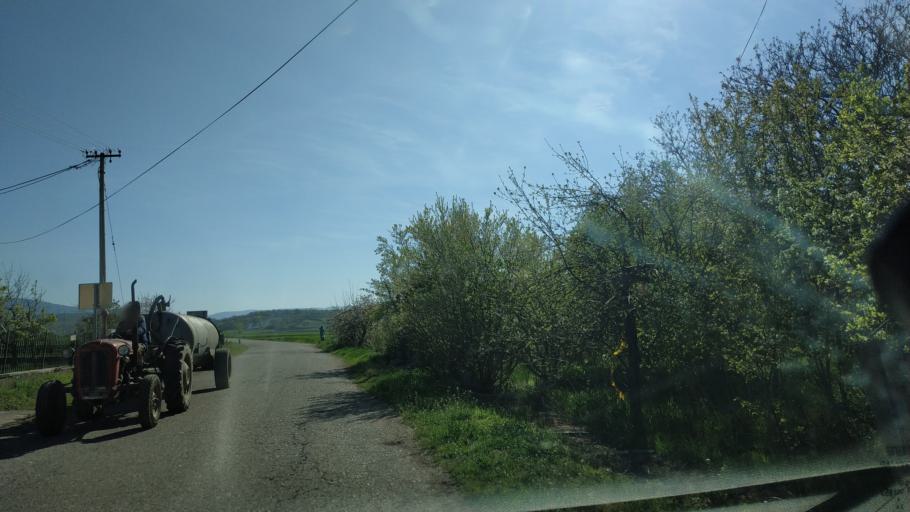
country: RS
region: Central Serbia
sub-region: Nisavski Okrug
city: Aleksinac
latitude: 43.5072
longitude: 21.6836
